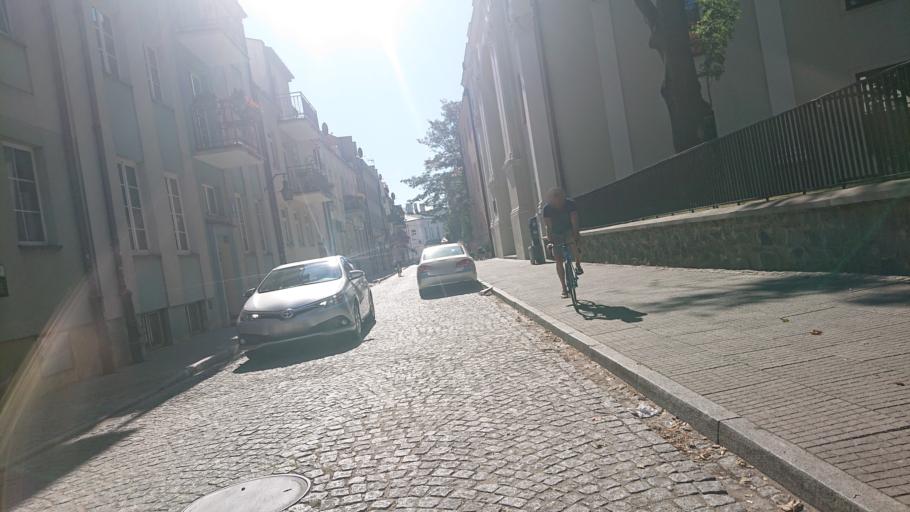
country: PL
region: Masovian Voivodeship
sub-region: Plock
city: Plock
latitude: 52.5441
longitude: 19.6859
